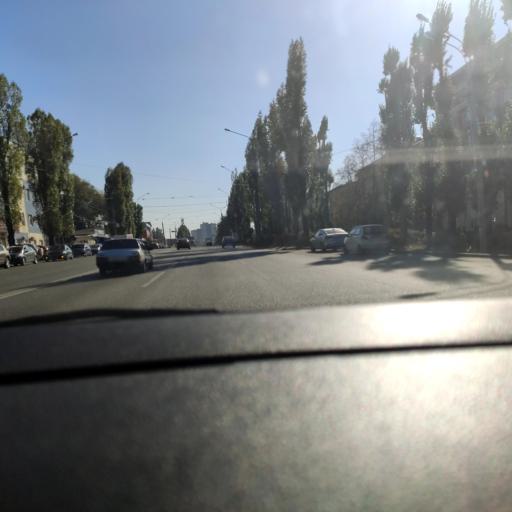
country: RU
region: Voronezj
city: Voronezh
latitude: 51.6889
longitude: 39.1652
